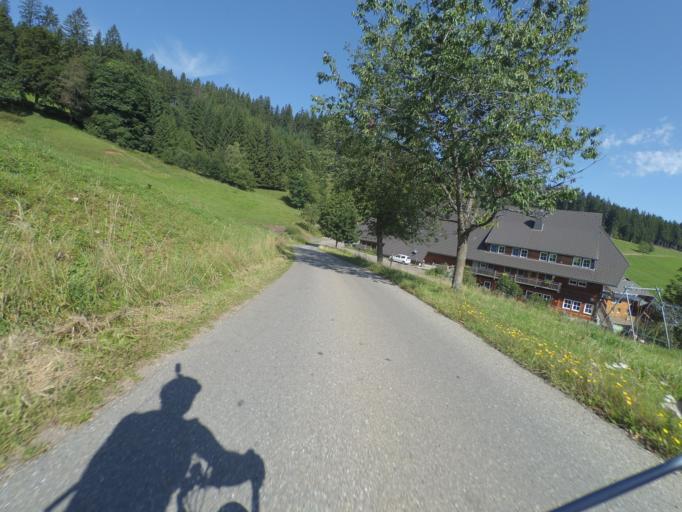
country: DE
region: Baden-Wuerttemberg
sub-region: Freiburg Region
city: Hinterzarten
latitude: 47.9387
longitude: 8.1334
